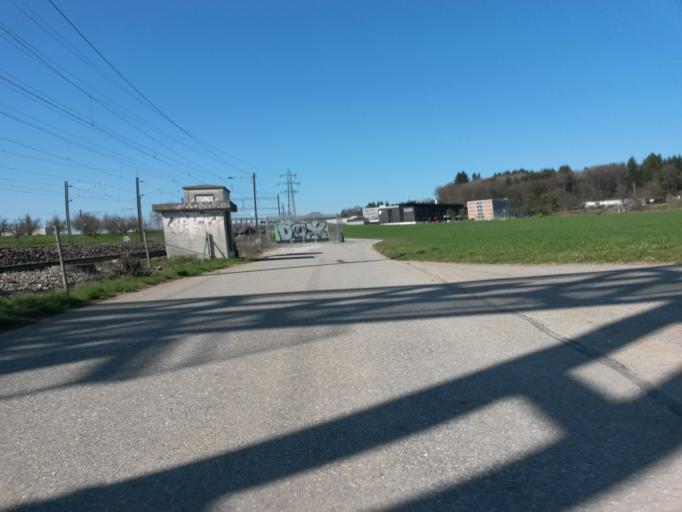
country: CH
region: Bern
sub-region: Bern-Mittelland District
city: Zollikofen
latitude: 46.9881
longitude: 7.4663
